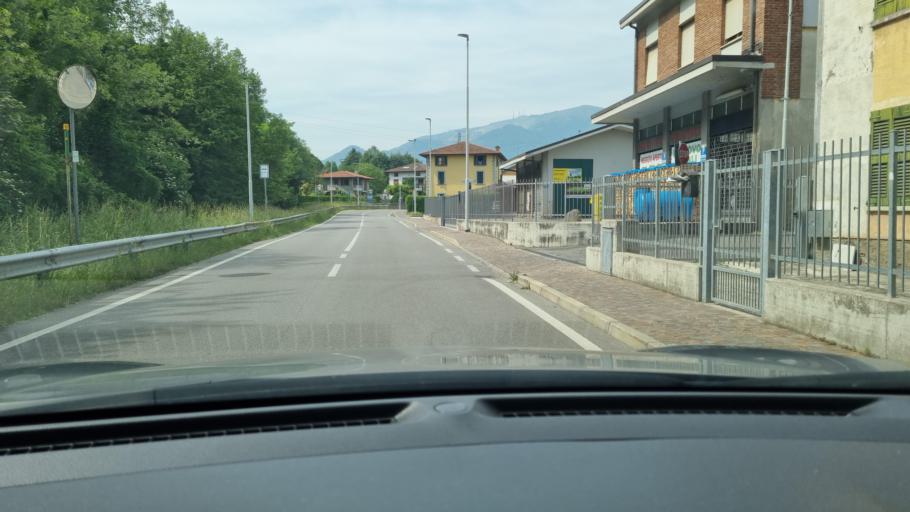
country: IT
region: Lombardy
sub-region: Provincia di Bergamo
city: Mapello
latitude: 45.7115
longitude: 9.5485
